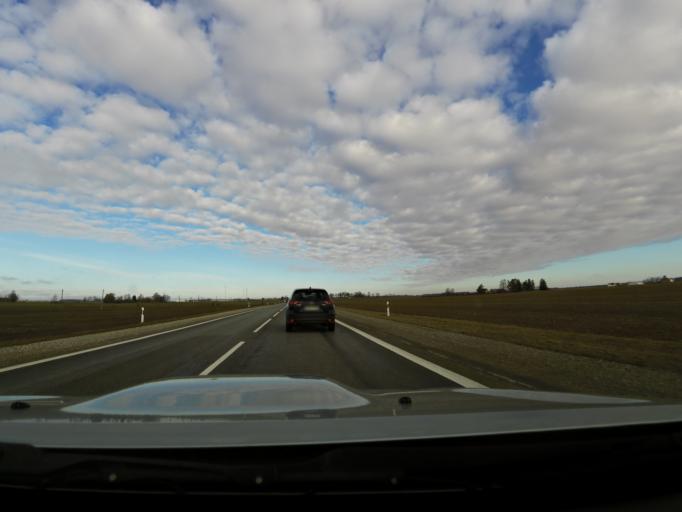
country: LT
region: Siauliu apskritis
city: Pakruojis
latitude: 55.7798
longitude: 24.0475
